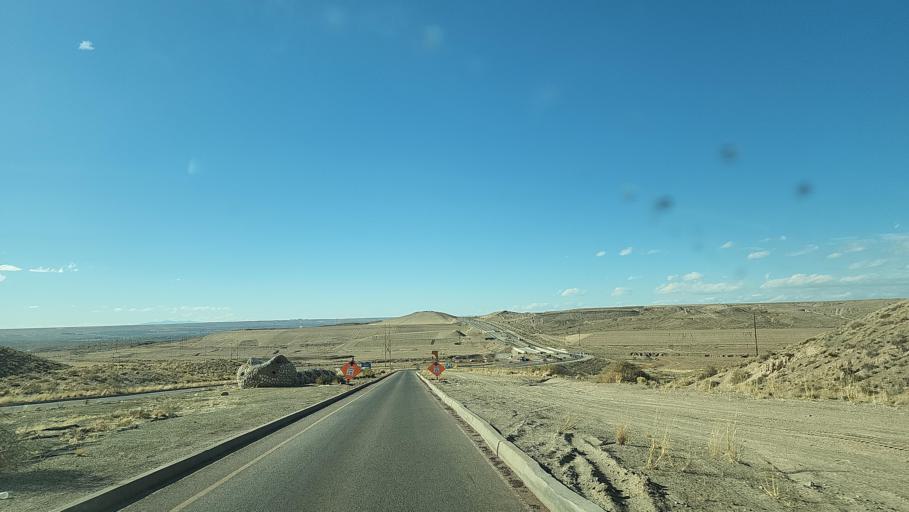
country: US
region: New Mexico
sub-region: Bernalillo County
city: South Valley
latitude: 35.0057
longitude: -106.6234
